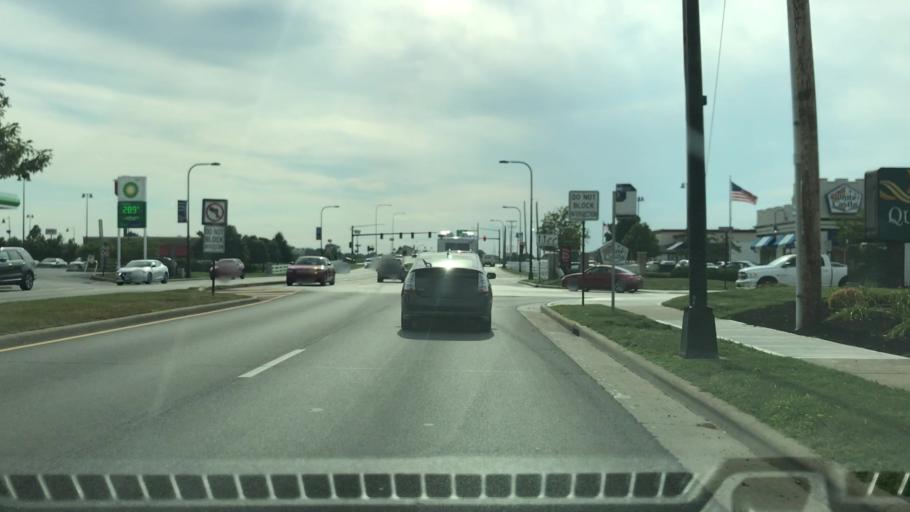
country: US
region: Ohio
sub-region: Franklin County
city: Grove City
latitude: 39.8788
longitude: -83.0452
